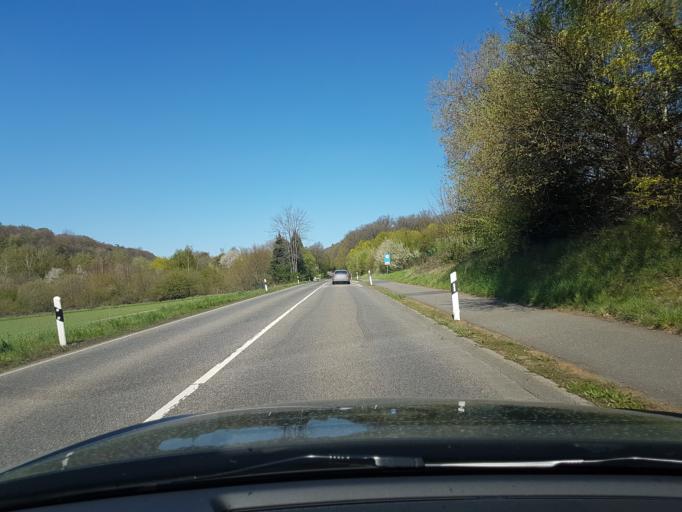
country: DE
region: Hesse
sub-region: Regierungsbezirk Darmstadt
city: Niedernhausen
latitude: 50.1670
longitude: 8.3076
